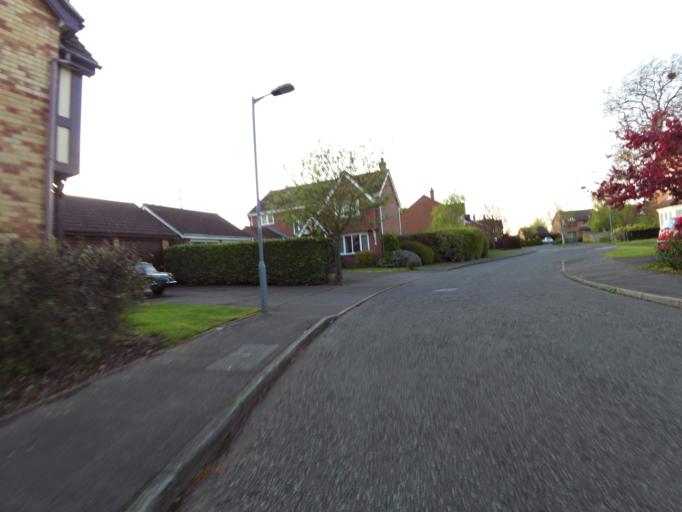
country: GB
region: England
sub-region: Suffolk
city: Ipswich
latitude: 52.0724
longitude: 1.1823
